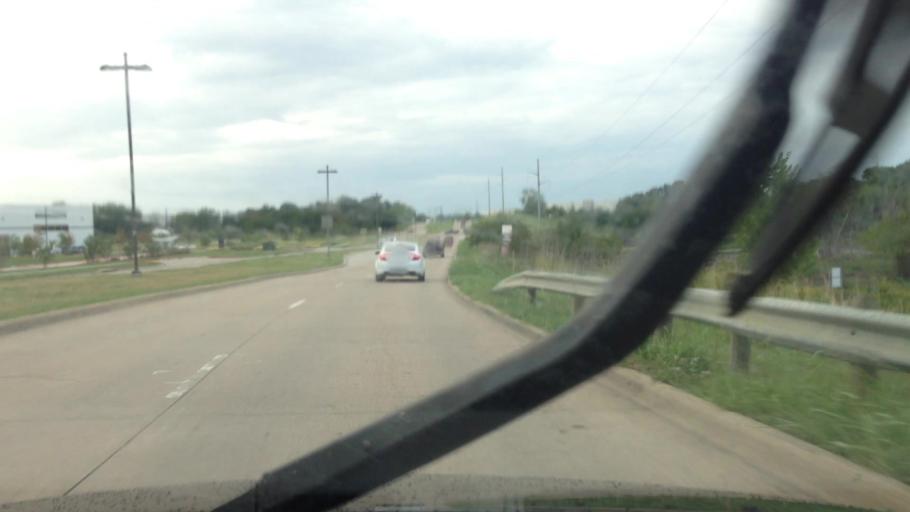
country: US
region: Texas
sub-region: Dallas County
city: Coppell
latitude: 32.9859
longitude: -97.0282
